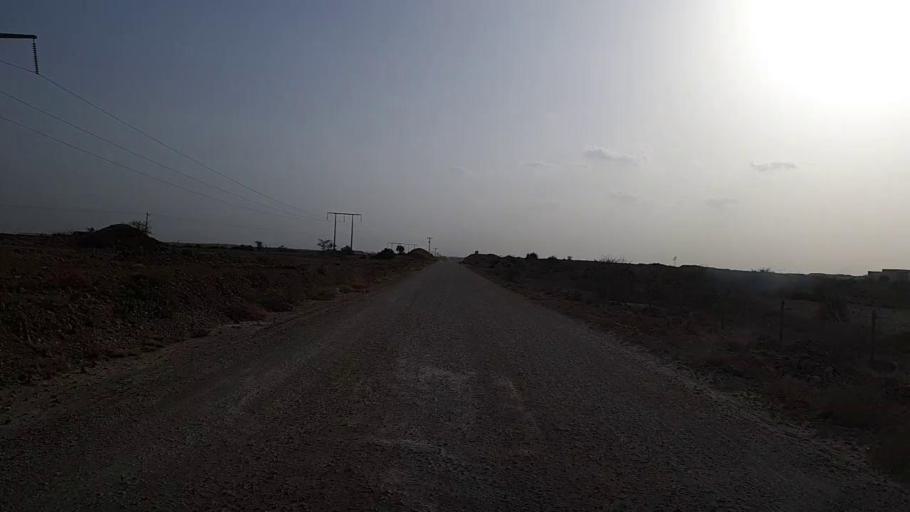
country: PK
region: Sindh
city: Thatta
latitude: 25.1964
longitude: 67.8713
